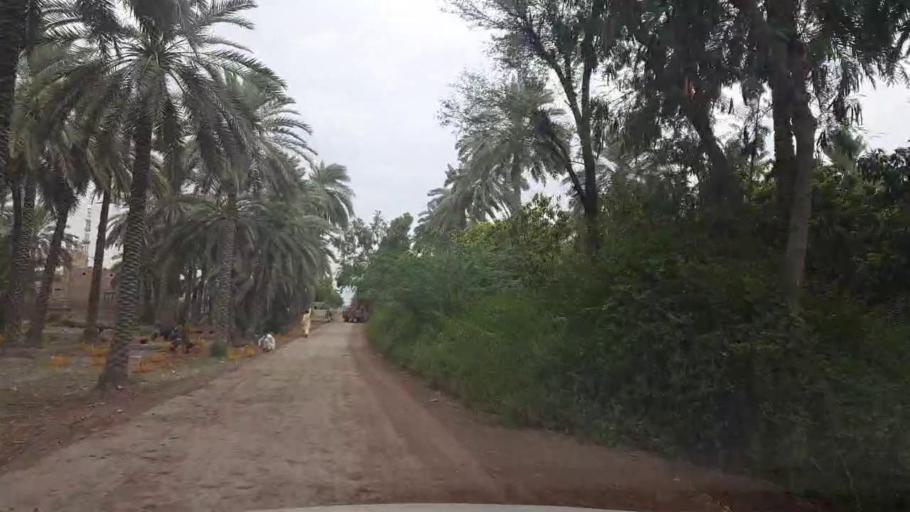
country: PK
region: Sindh
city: Khairpur
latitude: 27.5937
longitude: 68.8139
